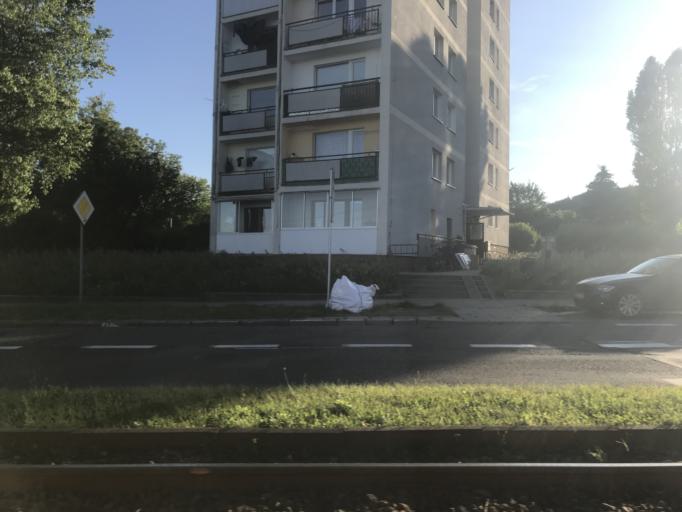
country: PL
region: Pomeranian Voivodeship
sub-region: Sopot
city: Sopot
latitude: 54.3972
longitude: 18.5703
